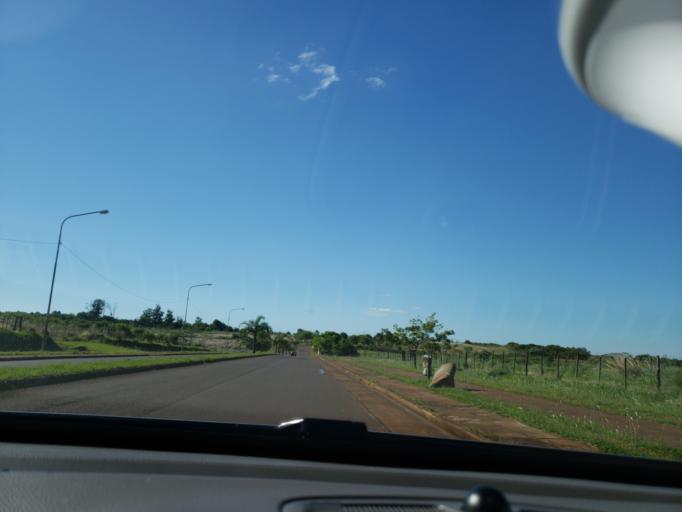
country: AR
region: Misiones
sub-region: Departamento de Capital
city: Posadas
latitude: -27.3862
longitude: -55.9619
